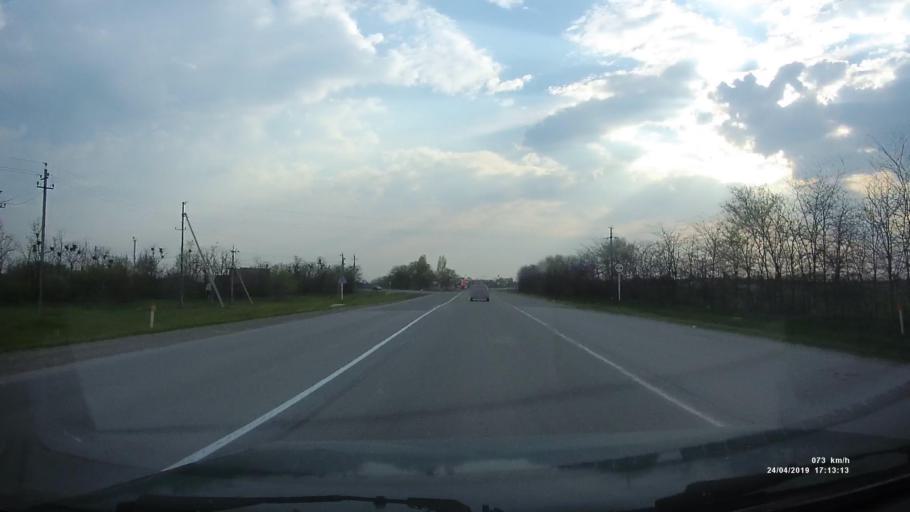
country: RU
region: Rostov
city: Sal'sk
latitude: 46.4787
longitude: 41.4789
